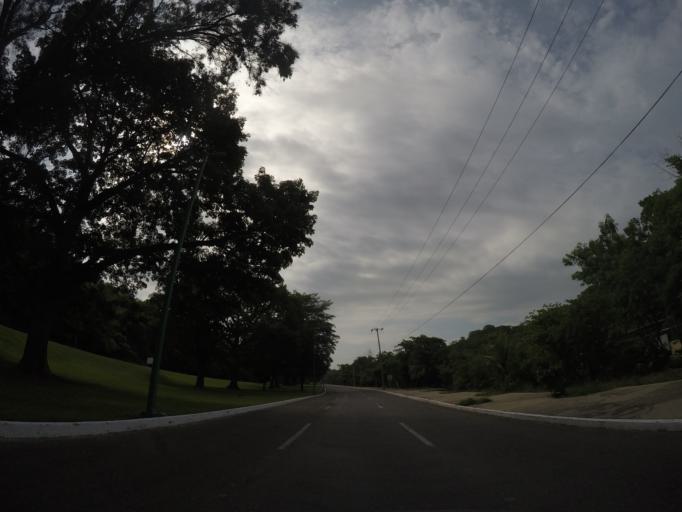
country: MX
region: Oaxaca
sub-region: Santa Maria Huatulco
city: Sector H Tres
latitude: 15.7779
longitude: -96.1512
